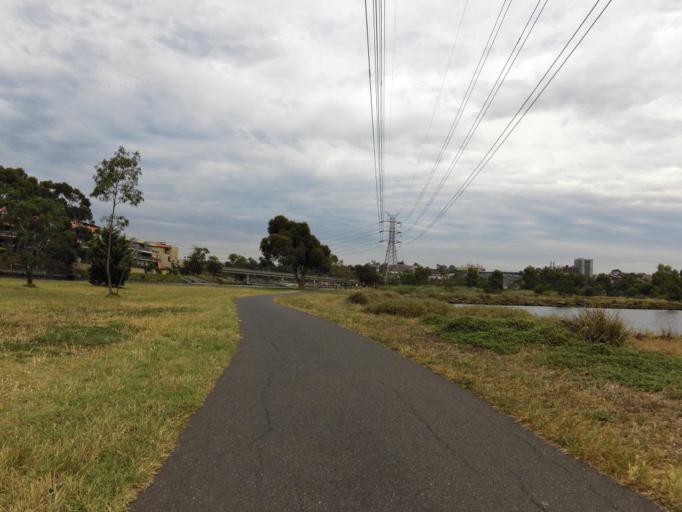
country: AU
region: Victoria
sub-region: Maribyrnong
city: Footscray
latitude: -37.7871
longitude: 144.9030
